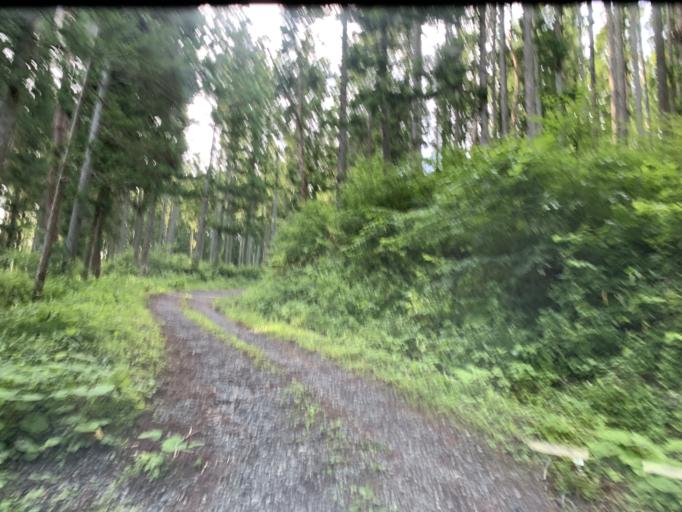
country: JP
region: Iwate
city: Ichinoseki
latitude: 38.8989
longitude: 140.9517
